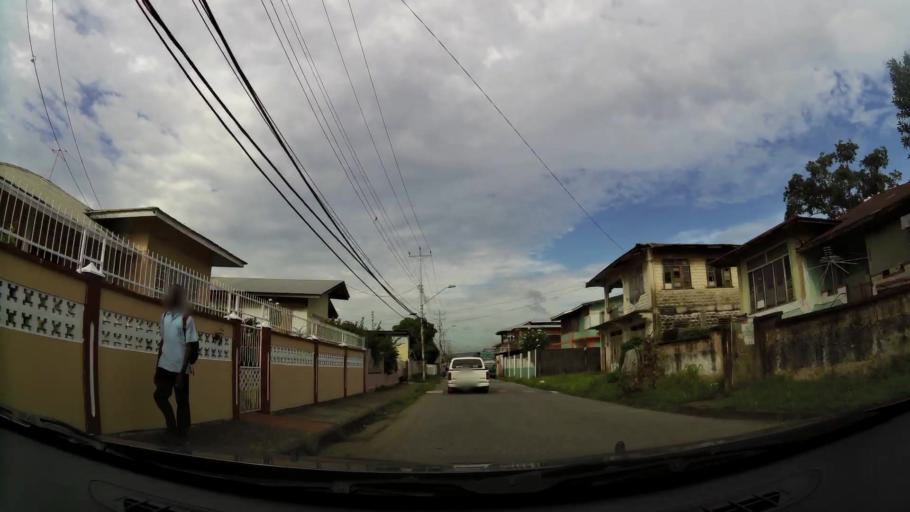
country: TT
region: San Juan/Laventille
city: Laventille
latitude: 10.6538
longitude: -61.4461
